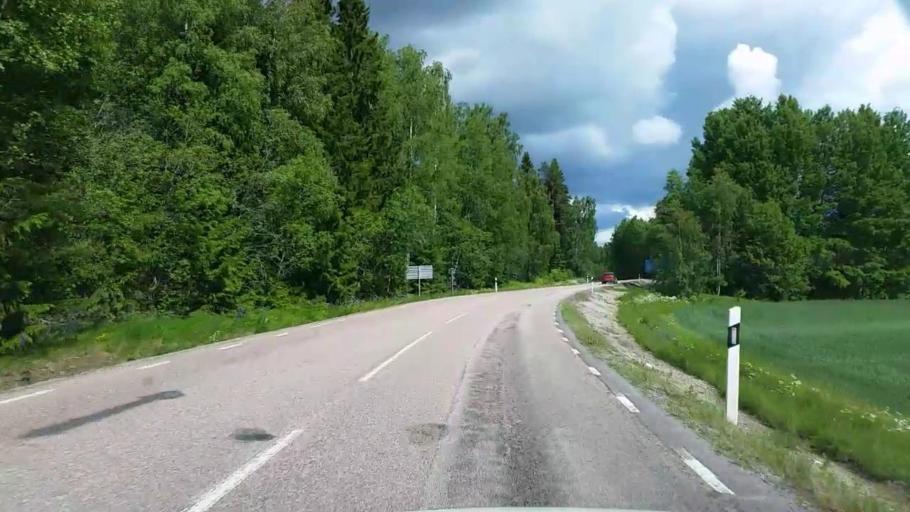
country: SE
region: Vaestmanland
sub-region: Skinnskattebergs Kommun
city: Skinnskatteberg
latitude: 59.7992
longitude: 15.8457
